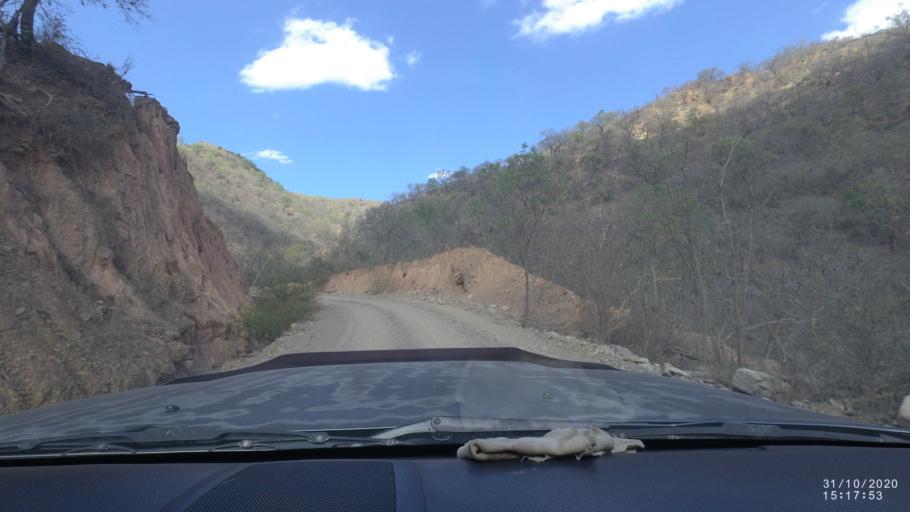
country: BO
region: Cochabamba
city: Aiquile
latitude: -18.3416
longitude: -64.7654
